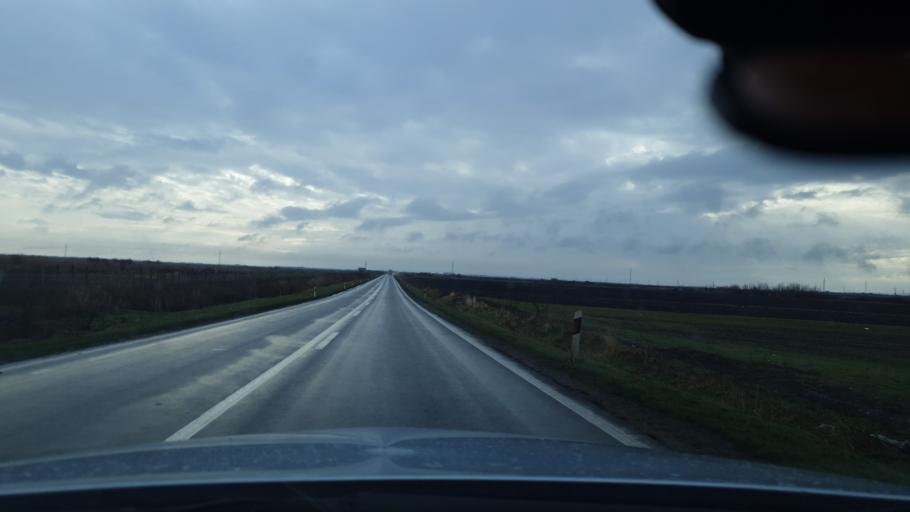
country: RS
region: Autonomna Pokrajina Vojvodina
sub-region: Juznobanatski Okrug
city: Kovin
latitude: 44.8046
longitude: 20.8973
